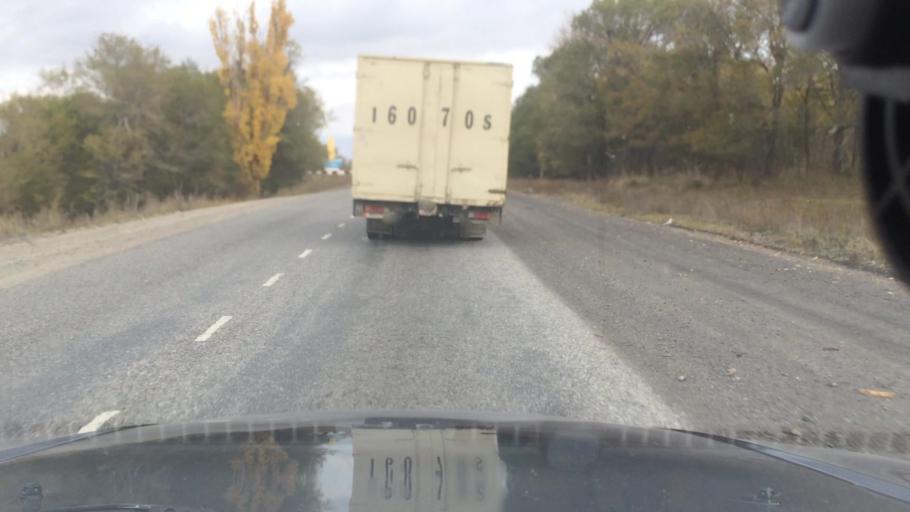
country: KG
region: Ysyk-Koel
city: Tyup
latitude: 42.6648
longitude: 78.3497
